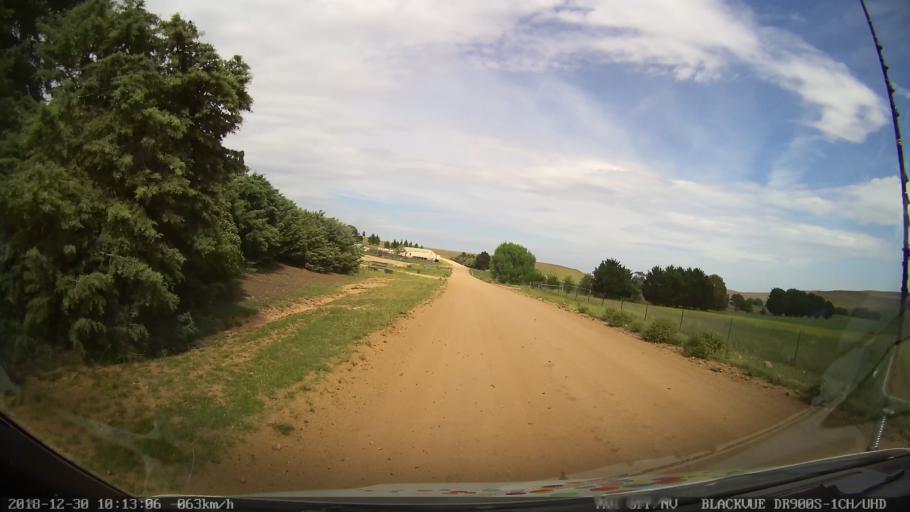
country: AU
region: New South Wales
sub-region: Snowy River
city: Berridale
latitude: -36.5381
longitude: 149.0693
